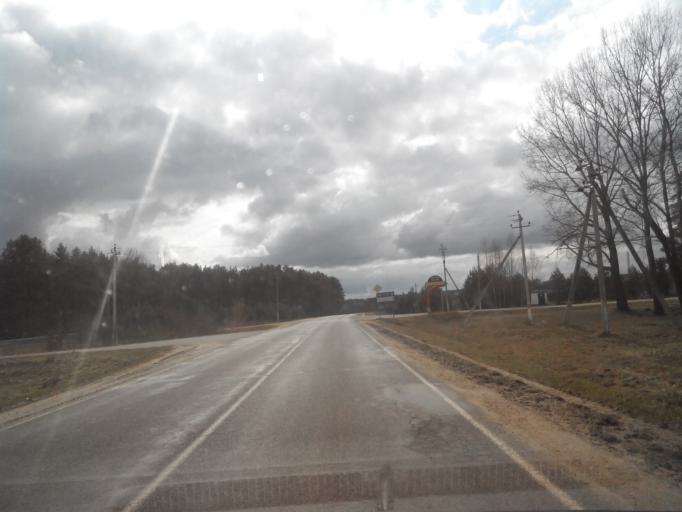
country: BY
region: Vitebsk
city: Pastavy
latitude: 55.1005
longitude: 26.8586
